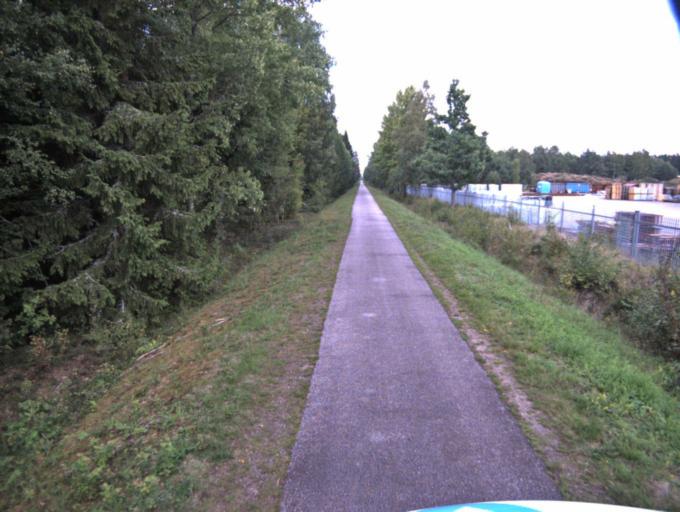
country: SE
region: Vaestra Goetaland
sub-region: Ulricehamns Kommun
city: Ulricehamn
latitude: 57.8267
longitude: 13.4178
